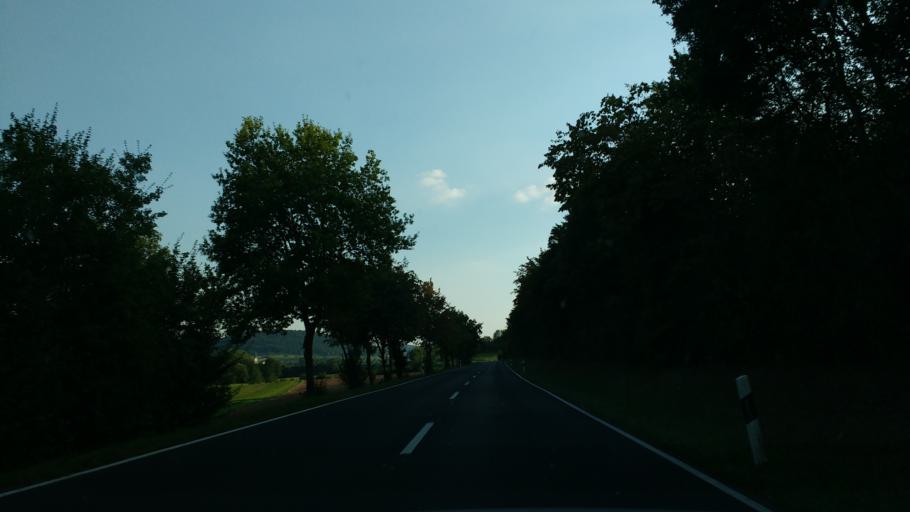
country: DE
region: Bavaria
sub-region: Regierungsbezirk Unterfranken
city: Elfershausen
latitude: 50.1407
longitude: 9.9471
